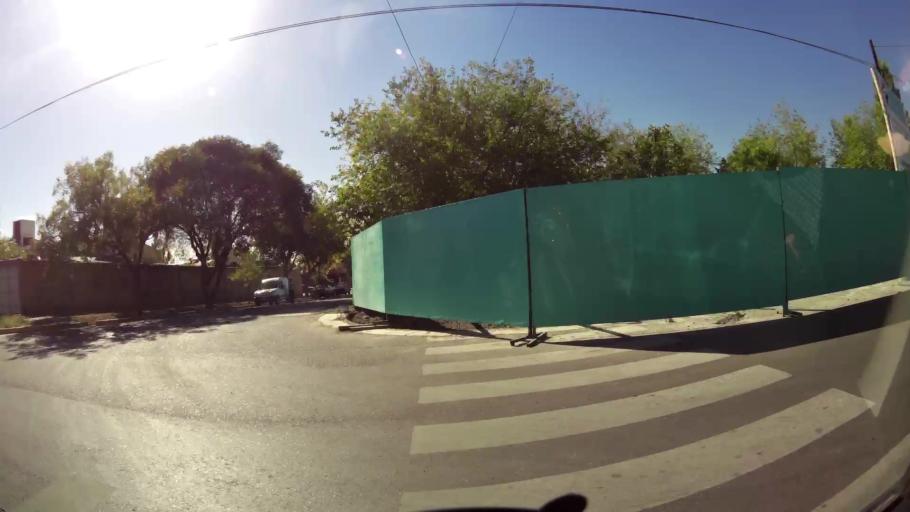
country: AR
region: Mendoza
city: Mendoza
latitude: -32.8771
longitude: -68.8731
